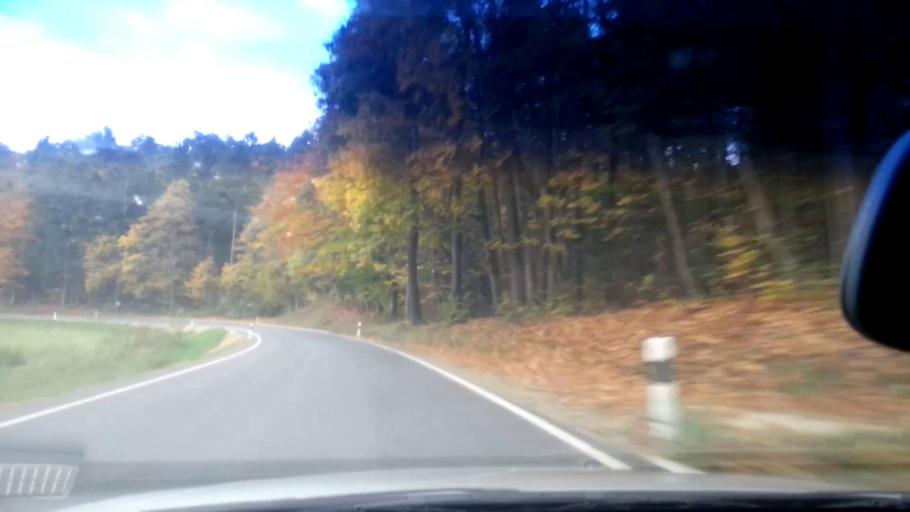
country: DE
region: Bavaria
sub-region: Upper Franconia
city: Wonsees
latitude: 49.9855
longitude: 11.2962
